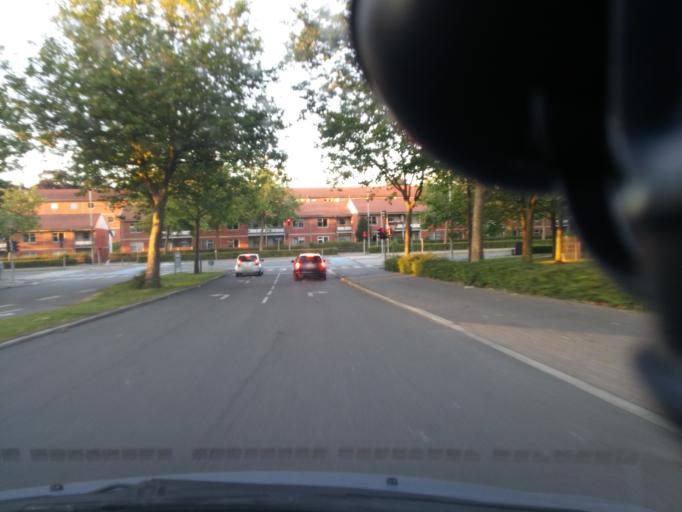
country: DK
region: South Denmark
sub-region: Odense Kommune
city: Odense
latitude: 55.4032
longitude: 10.3882
